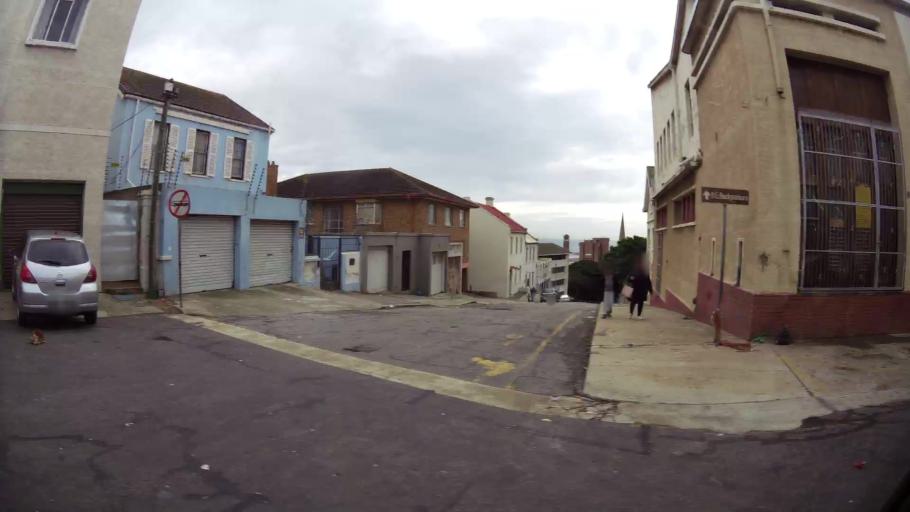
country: ZA
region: Eastern Cape
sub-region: Nelson Mandela Bay Metropolitan Municipality
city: Port Elizabeth
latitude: -33.9634
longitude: 25.6210
